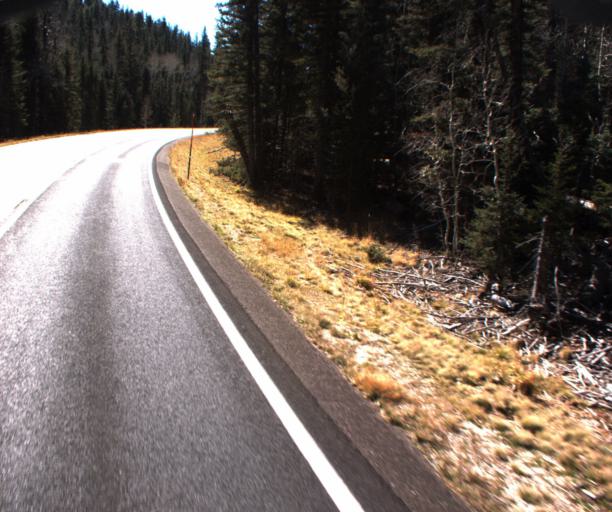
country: US
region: Arizona
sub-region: Coconino County
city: Grand Canyon
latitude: 36.5207
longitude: -112.1394
